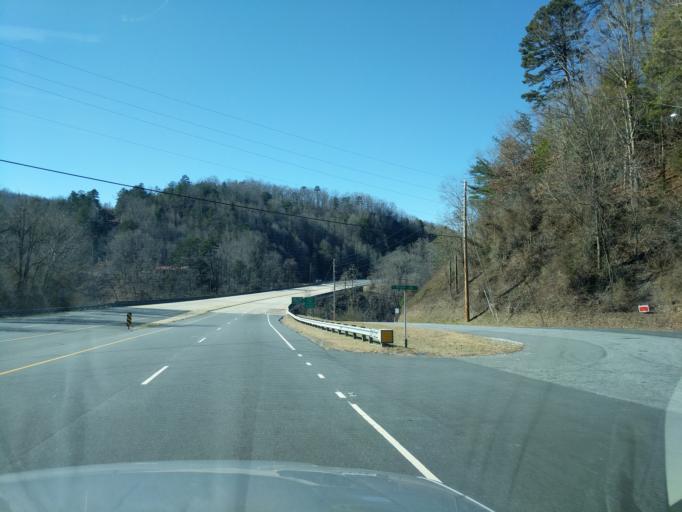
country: US
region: North Carolina
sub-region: Swain County
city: Bryson City
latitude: 35.3745
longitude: -83.5172
